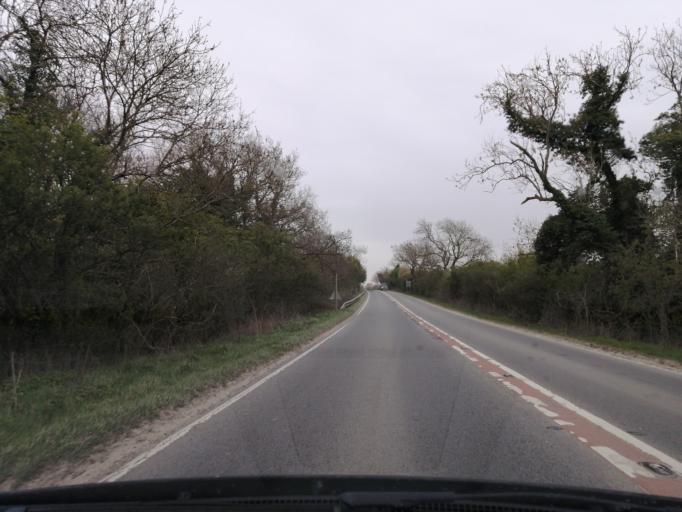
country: GB
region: England
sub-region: Peterborough
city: Wittering
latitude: 52.5916
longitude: -0.4563
